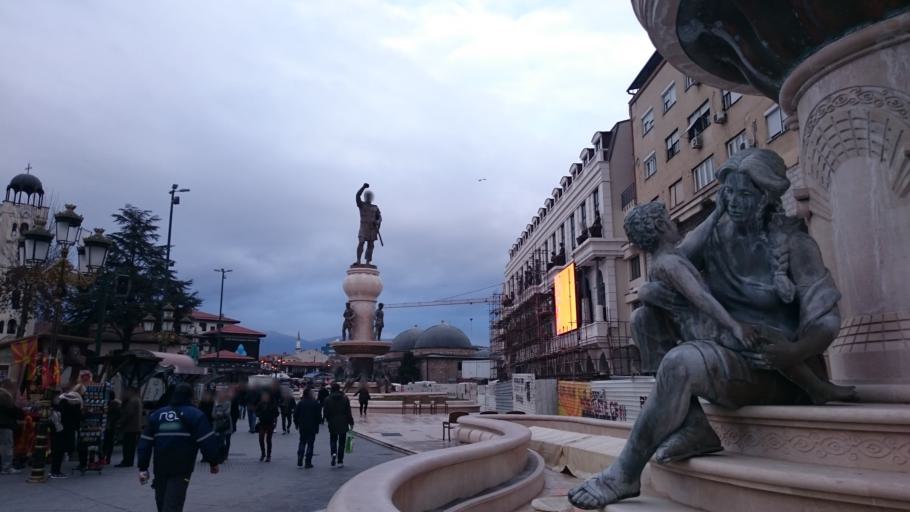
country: MK
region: Karpos
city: Skopje
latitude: 41.9979
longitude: 21.4342
